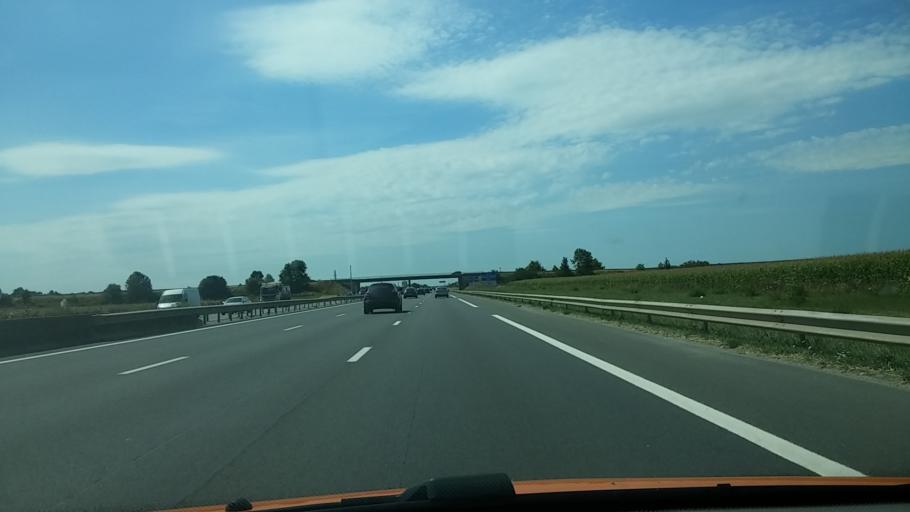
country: FR
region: Ile-de-France
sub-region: Departement de Seine-et-Marne
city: Serris
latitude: 48.8309
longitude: 2.7599
